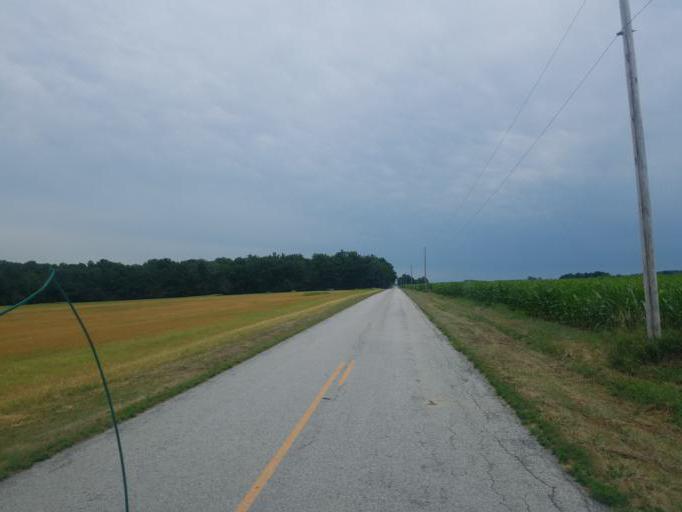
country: US
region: Ohio
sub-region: Defiance County
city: Hicksville
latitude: 41.2372
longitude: -84.7748
